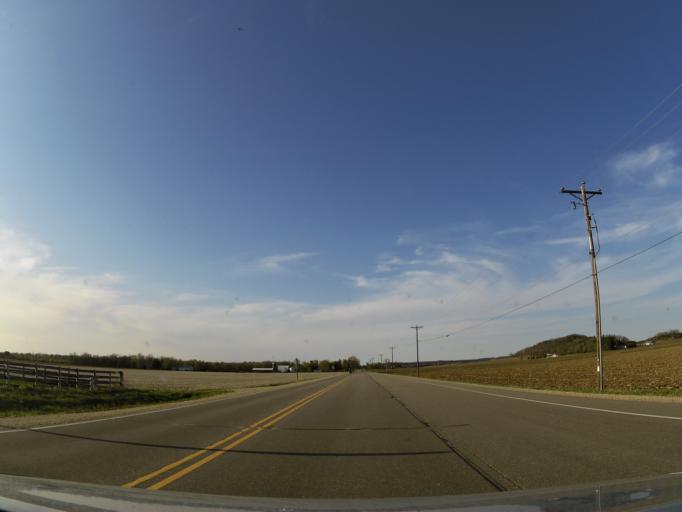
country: US
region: Minnesota
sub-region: Washington County
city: Afton
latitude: 44.8384
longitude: -92.7311
